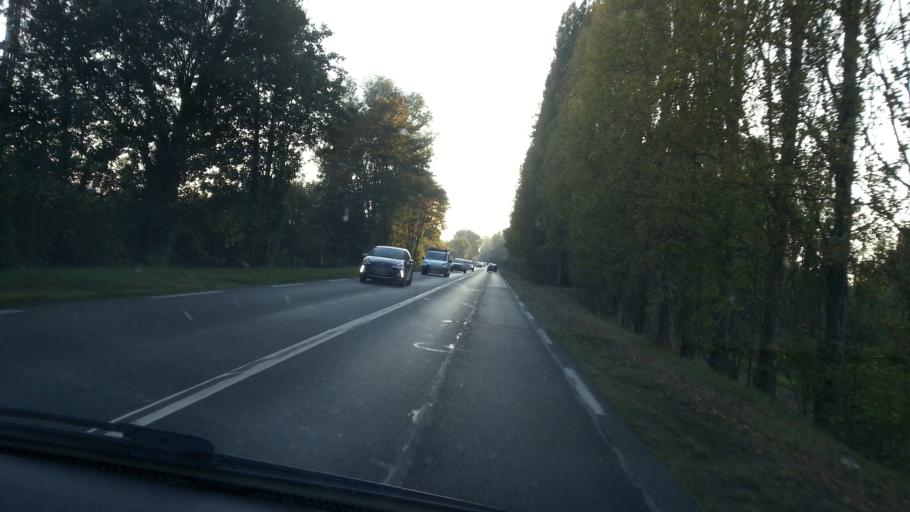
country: FR
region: Picardie
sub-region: Departement de l'Oise
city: Rieux
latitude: 49.2936
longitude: 2.5104
